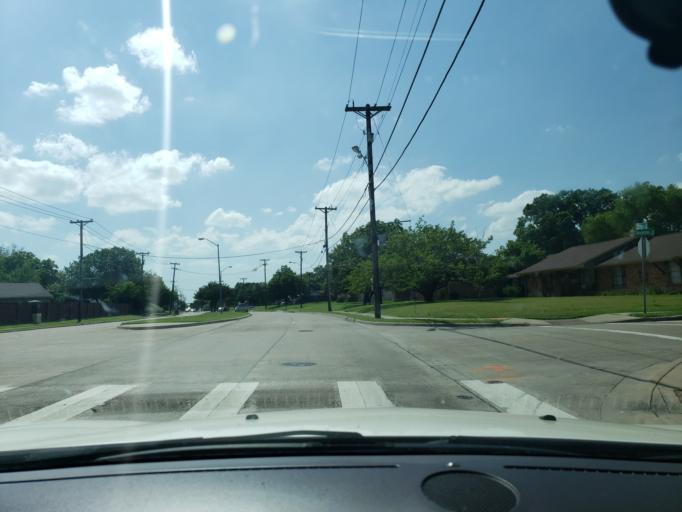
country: US
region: Texas
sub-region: Dallas County
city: Rowlett
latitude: 32.8937
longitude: -96.5610
